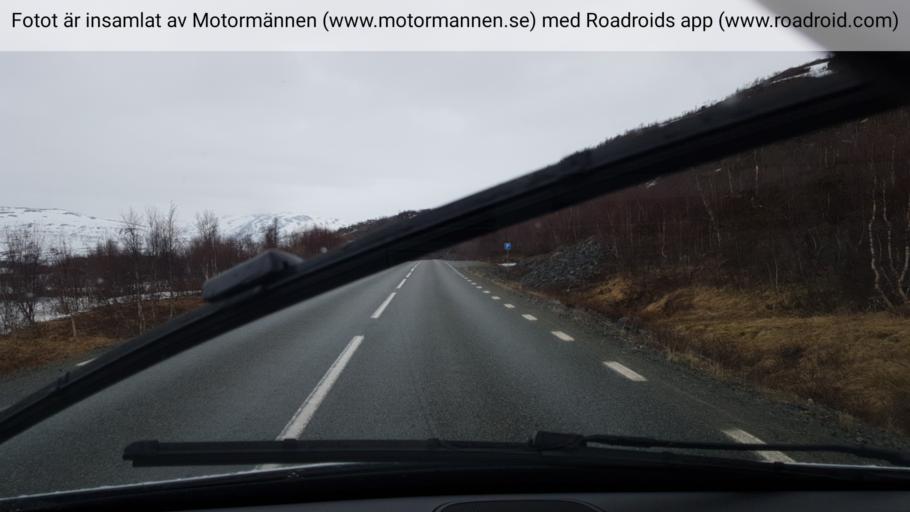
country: NO
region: Nordland
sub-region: Rana
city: Mo i Rana
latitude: 66.1281
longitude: 14.6018
